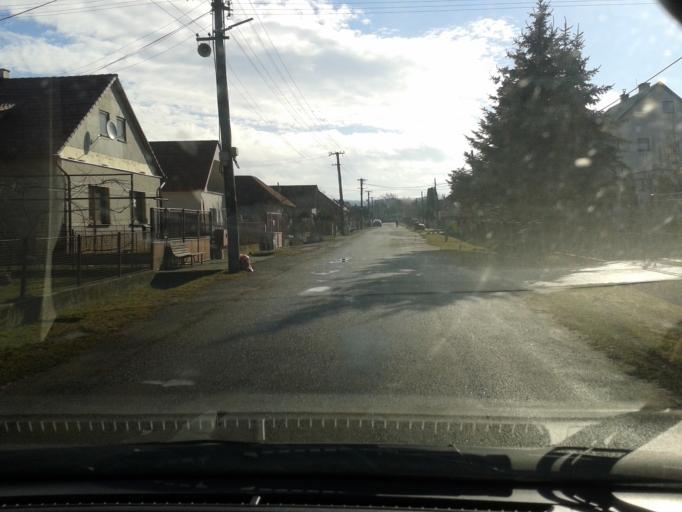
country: SK
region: Nitriansky
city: Levice
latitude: 48.2597
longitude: 18.7347
